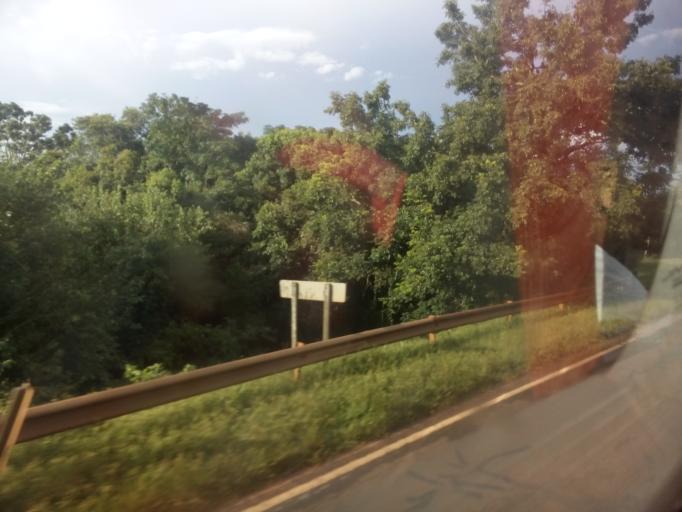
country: AR
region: Misiones
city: Santa Ana
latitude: -27.3873
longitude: -55.5933
